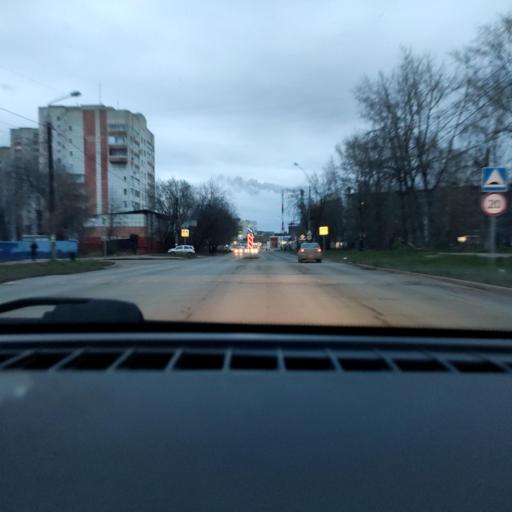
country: RU
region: Perm
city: Perm
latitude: 57.9739
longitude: 56.2393
